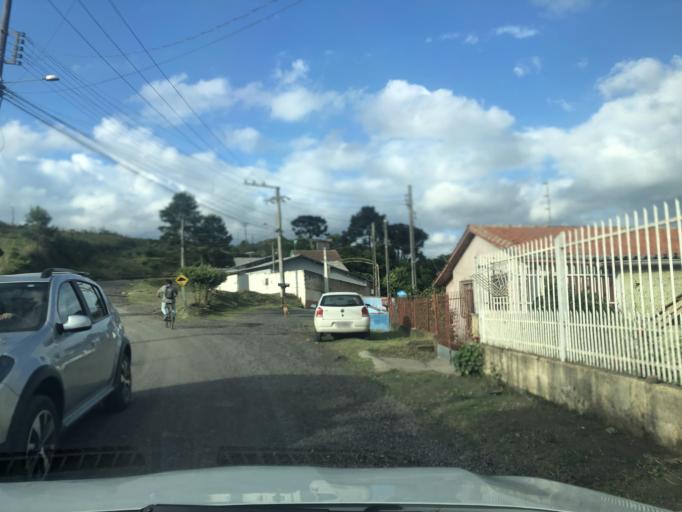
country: BR
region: Santa Catarina
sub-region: Lages
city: Lages
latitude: -27.7942
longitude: -50.3172
